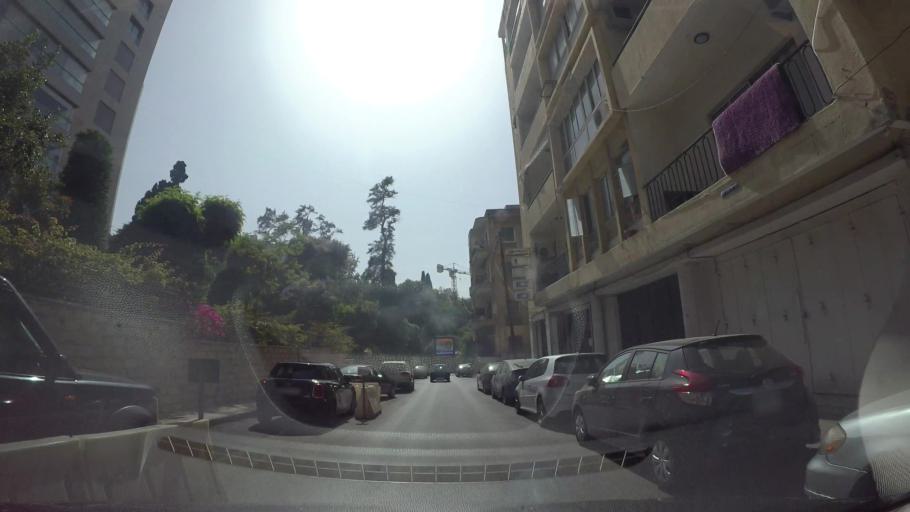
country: LB
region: Beyrouth
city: Ra's Bayrut
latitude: 33.8992
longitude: 35.4909
